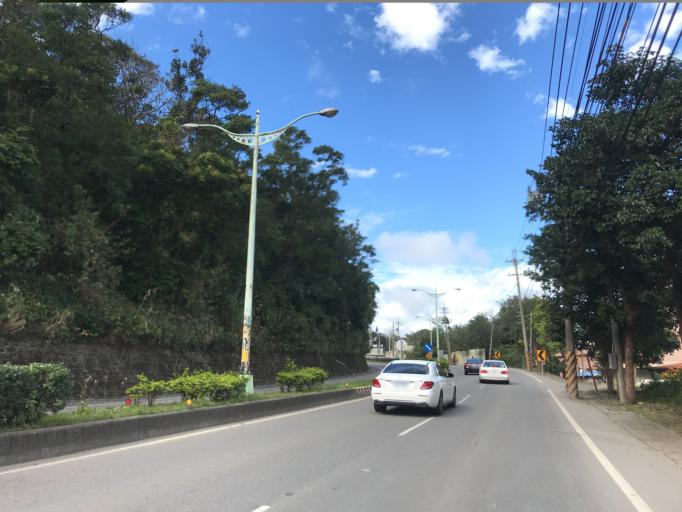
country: TW
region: Taiwan
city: Daxi
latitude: 24.8394
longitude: 121.2459
